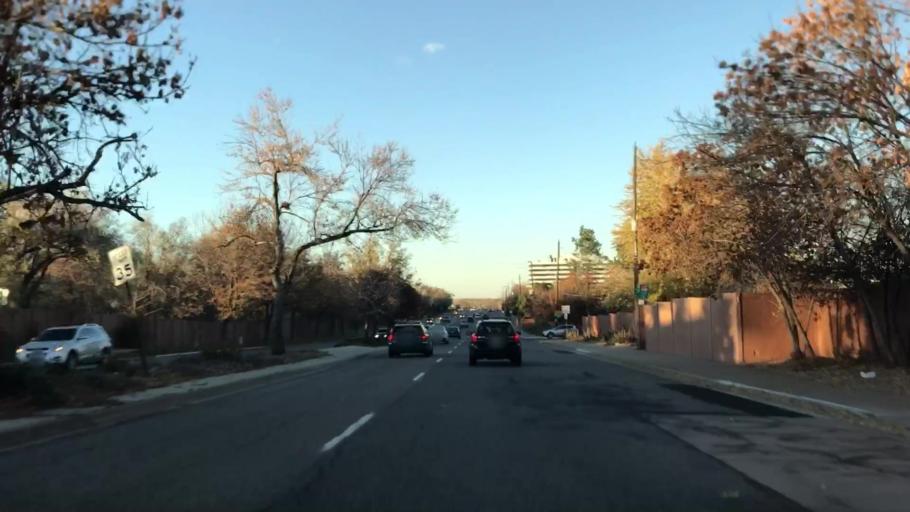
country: US
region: Colorado
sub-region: Arapahoe County
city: Castlewood
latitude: 39.6450
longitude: -104.8850
